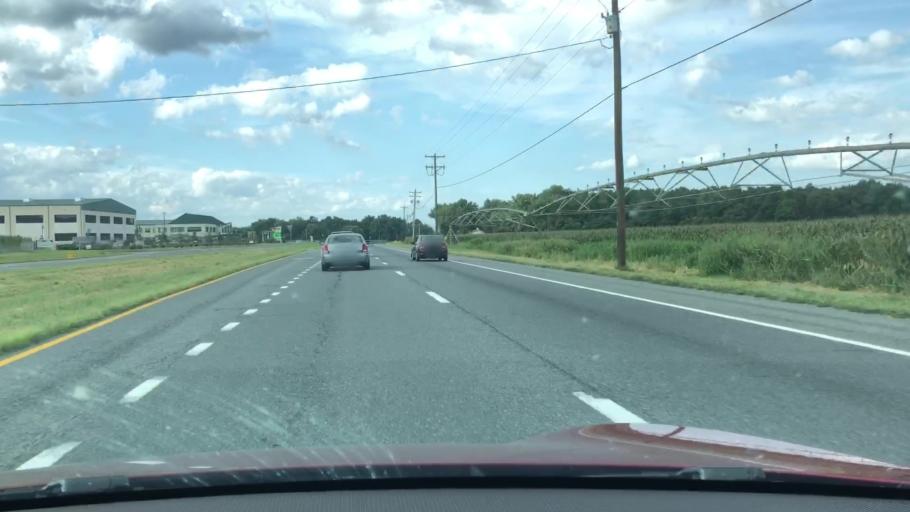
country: US
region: Delaware
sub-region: Sussex County
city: Bridgeville
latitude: 38.7895
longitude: -75.5897
